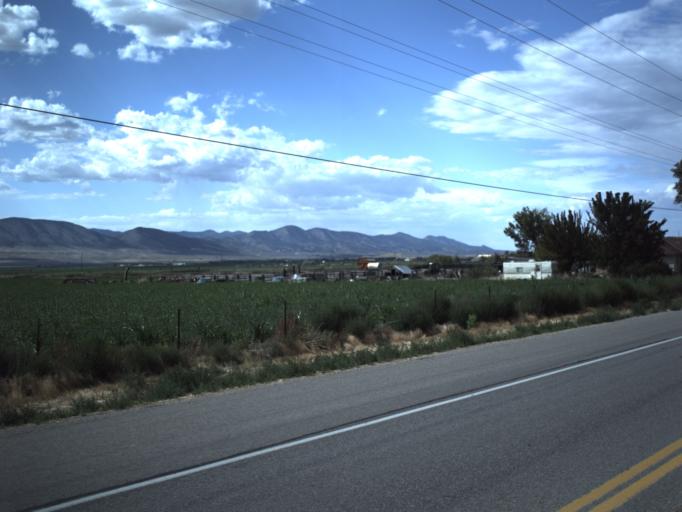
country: US
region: Utah
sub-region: Sanpete County
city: Centerfield
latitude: 39.1098
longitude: -111.8196
